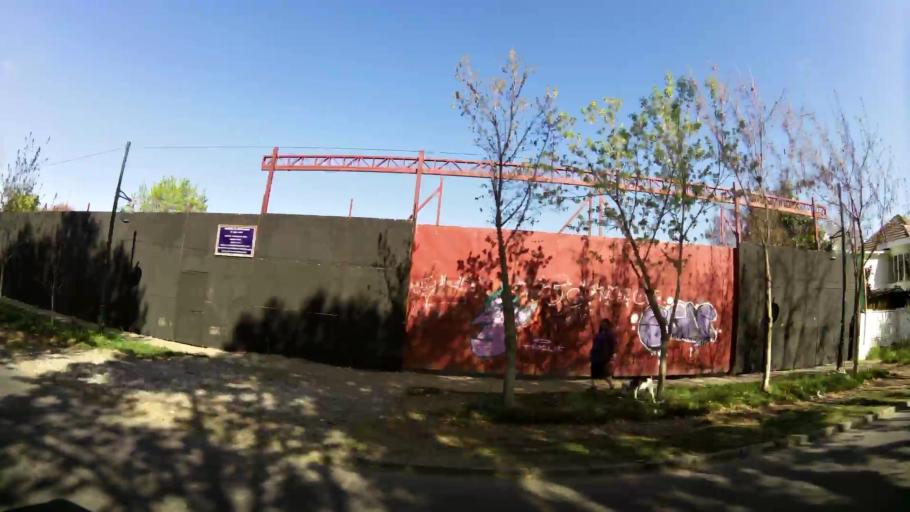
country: CL
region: Santiago Metropolitan
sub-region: Provincia de Santiago
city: Villa Presidente Frei, Nunoa, Santiago, Chile
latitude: -33.4468
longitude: -70.5770
